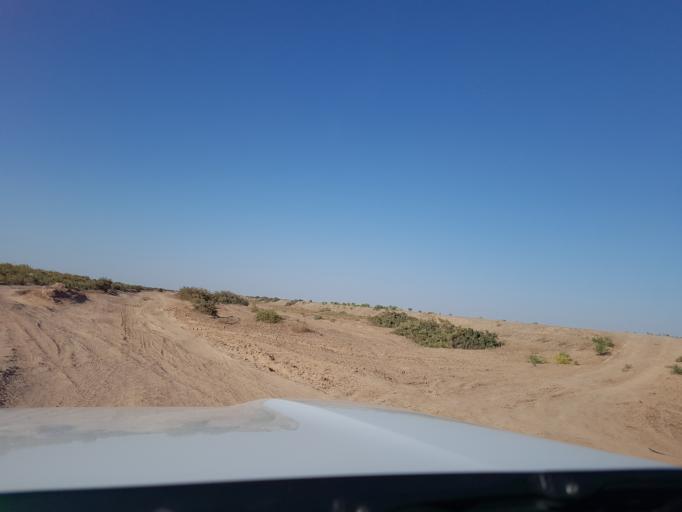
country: IR
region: Razavi Khorasan
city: Sarakhs
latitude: 36.9800
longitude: 61.3858
